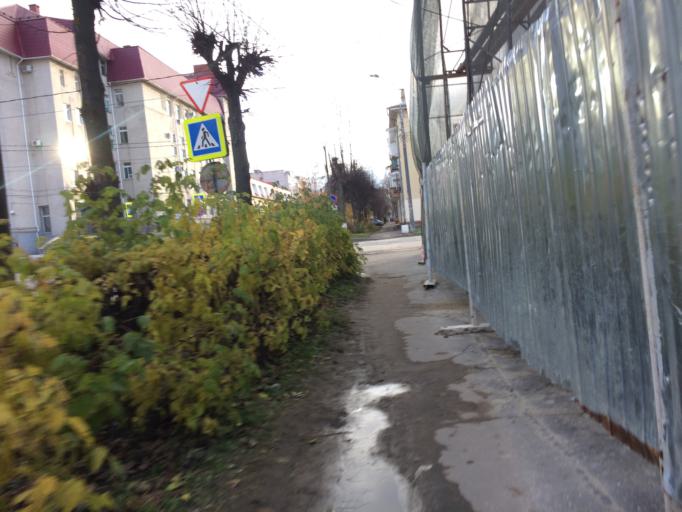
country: RU
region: Mariy-El
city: Yoshkar-Ola
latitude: 56.6384
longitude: 47.8971
